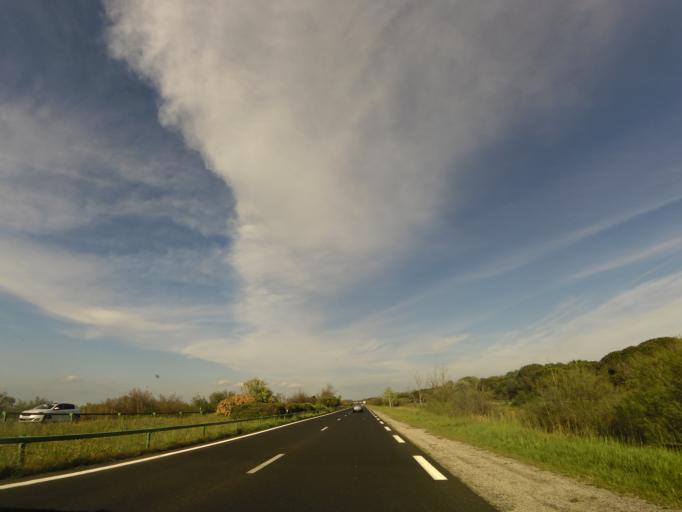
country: FR
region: Languedoc-Roussillon
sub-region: Departement de l'Herault
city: La Grande-Motte
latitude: 43.5678
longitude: 4.0658
